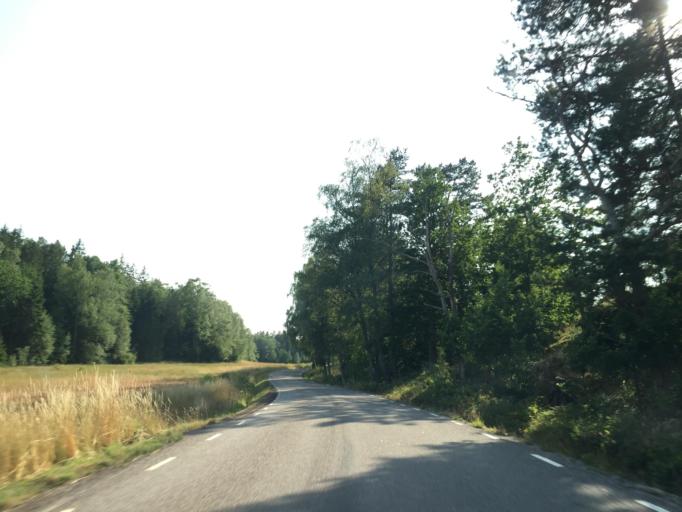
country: SE
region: Vaestra Goetaland
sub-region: Trollhattan
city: Trollhattan
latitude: 58.2691
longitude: 12.2438
